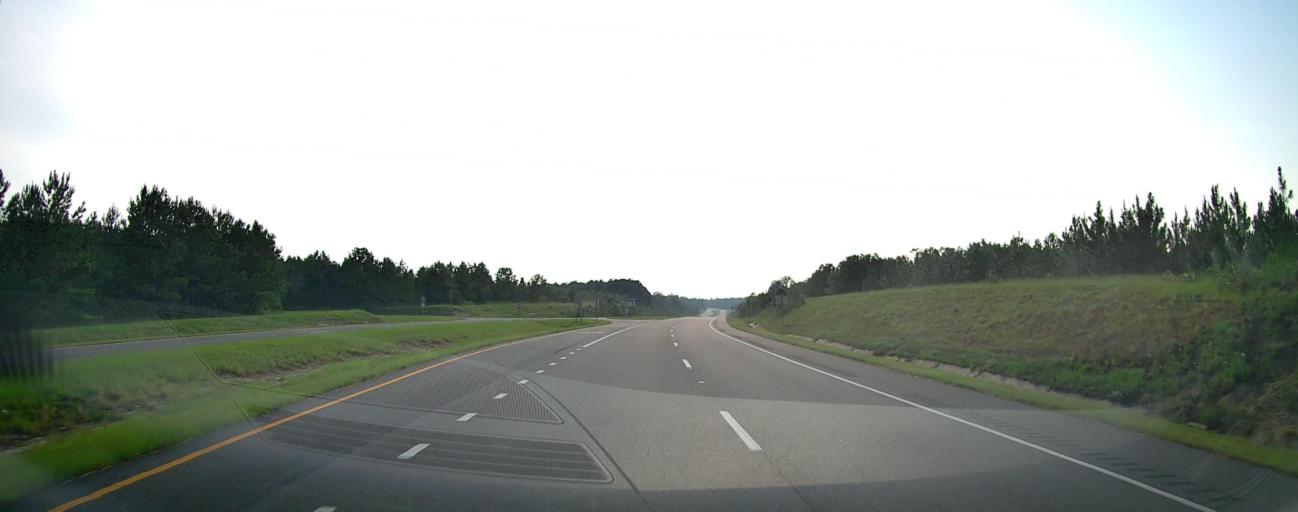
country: US
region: Georgia
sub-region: Talbot County
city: Talbotton
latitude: 32.5787
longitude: -84.5307
